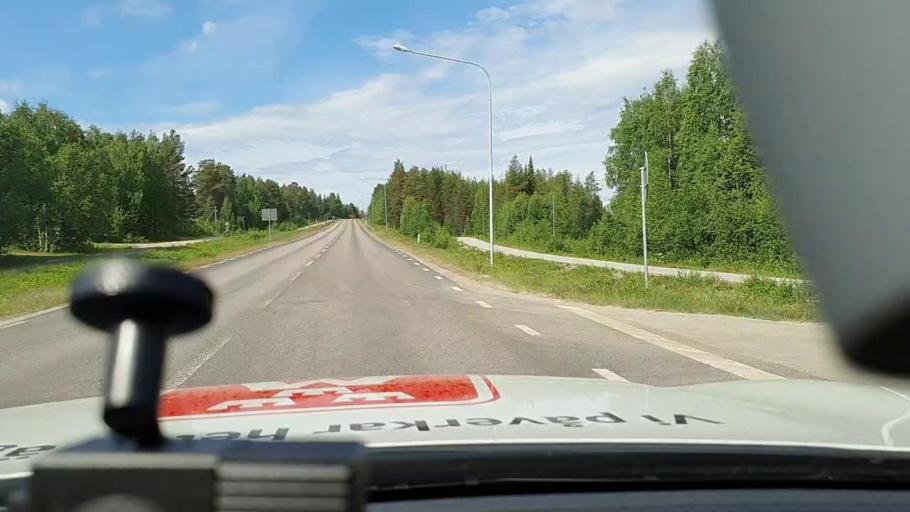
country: SE
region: Norrbotten
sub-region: Jokkmokks Kommun
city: Jokkmokk
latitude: 66.6026
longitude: 19.8633
